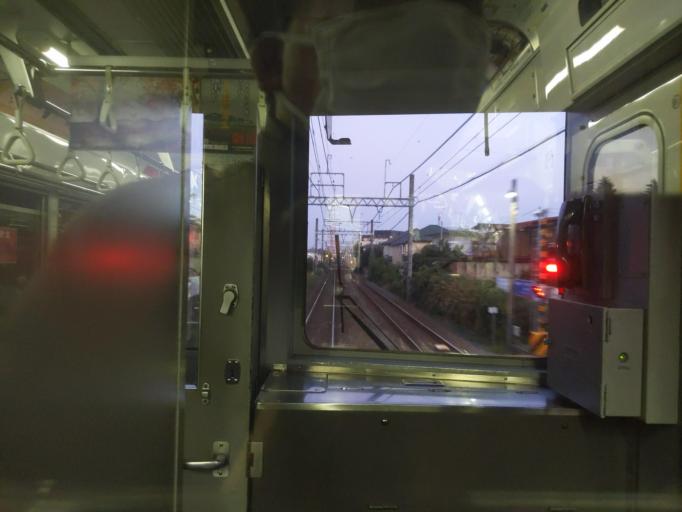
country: JP
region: Chiba
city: Kashiwa
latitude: 35.8602
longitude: 139.9601
